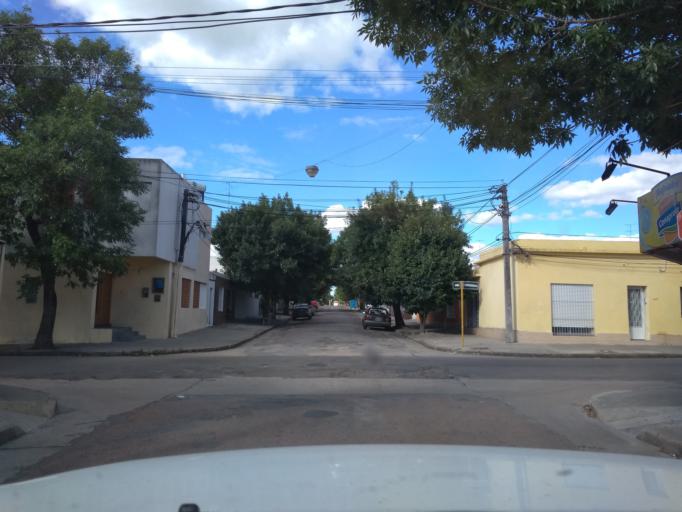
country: UY
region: Florida
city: Florida
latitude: -34.0932
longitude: -56.2218
